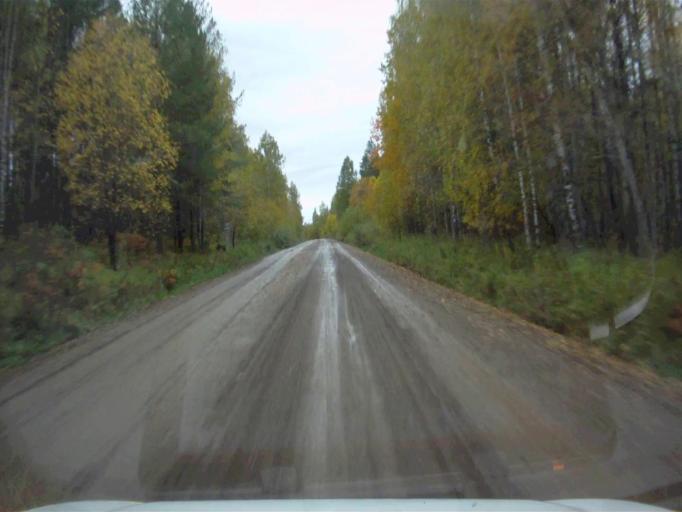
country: RU
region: Chelyabinsk
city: Nyazepetrovsk
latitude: 56.1061
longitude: 59.3827
